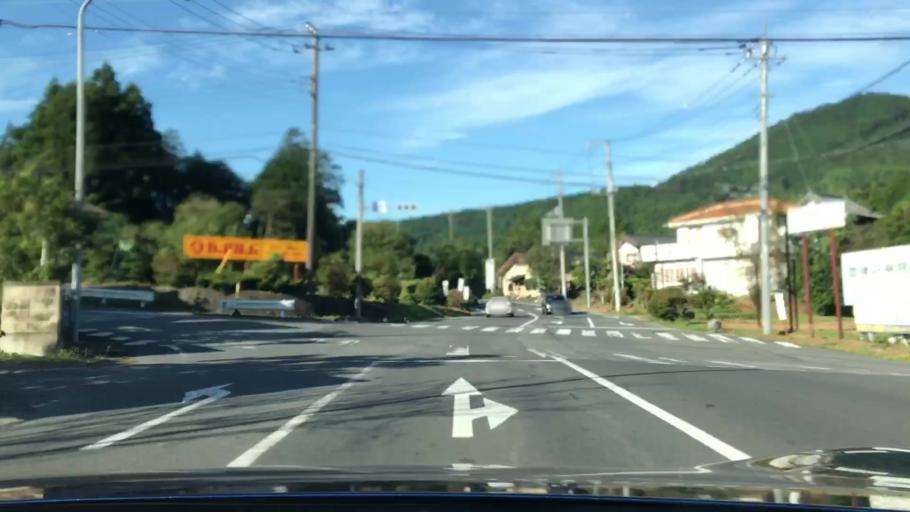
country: JP
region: Ibaraki
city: Makabe
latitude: 36.2511
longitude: 140.1661
